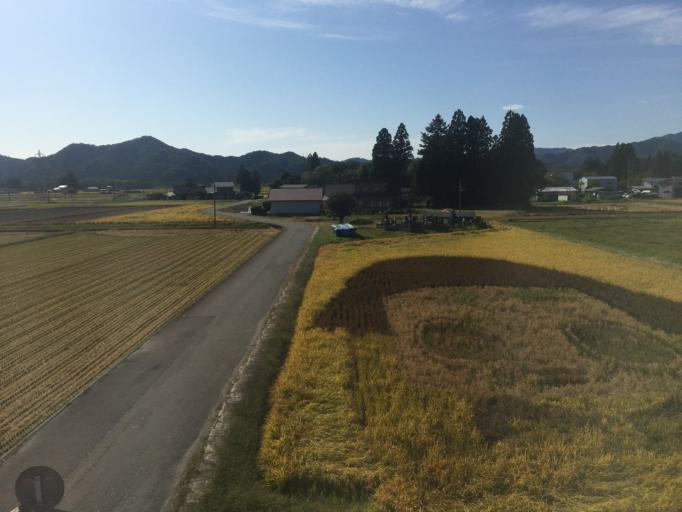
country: JP
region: Akita
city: Kakunodatemachi
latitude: 39.6199
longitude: 140.5749
